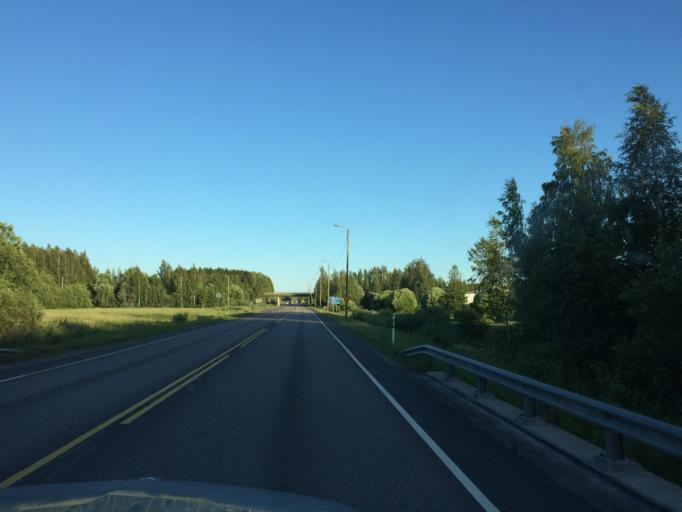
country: FI
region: Haeme
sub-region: Haemeenlinna
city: Tervakoski
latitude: 60.8207
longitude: 24.6377
